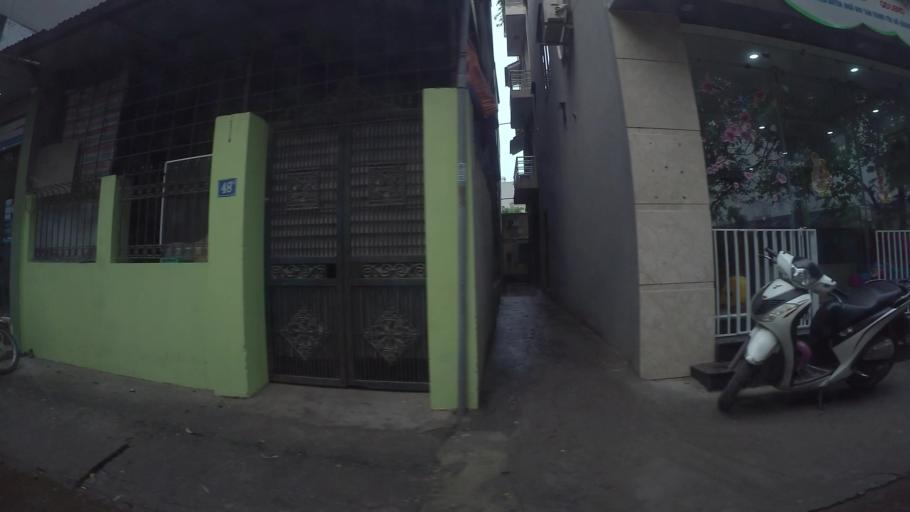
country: VN
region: Ha Noi
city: Van Dien
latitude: 20.9734
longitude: 105.8712
